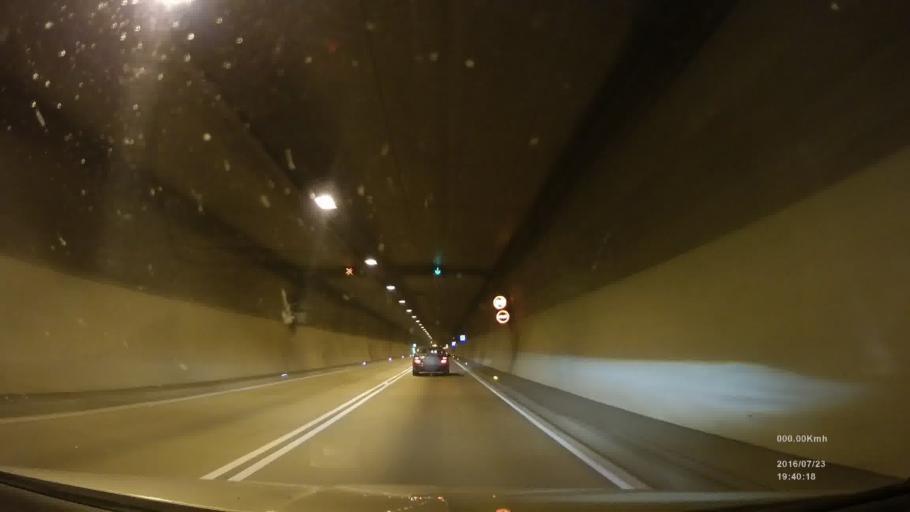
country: SK
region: Kosicky
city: Krompachy
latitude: 49.0030
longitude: 20.8779
